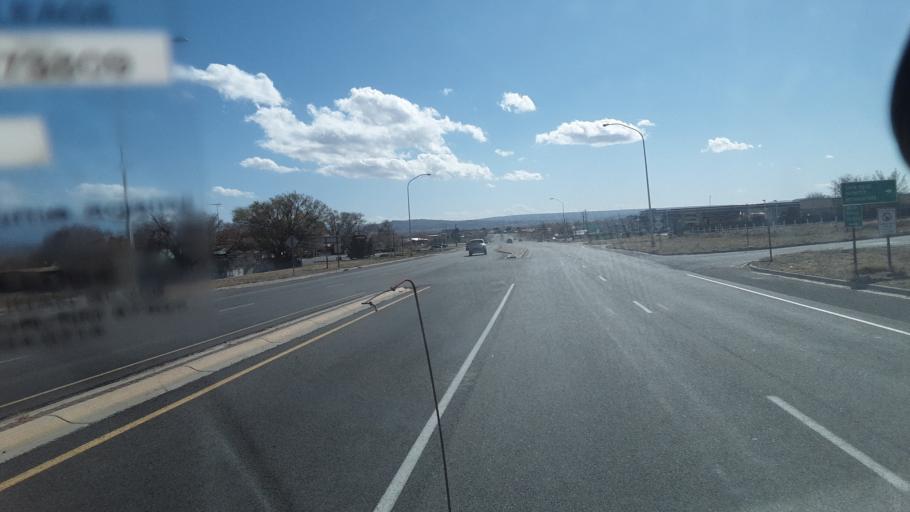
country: US
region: New Mexico
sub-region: Rio Arriba County
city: Espanola
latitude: 36.0110
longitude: -106.0887
